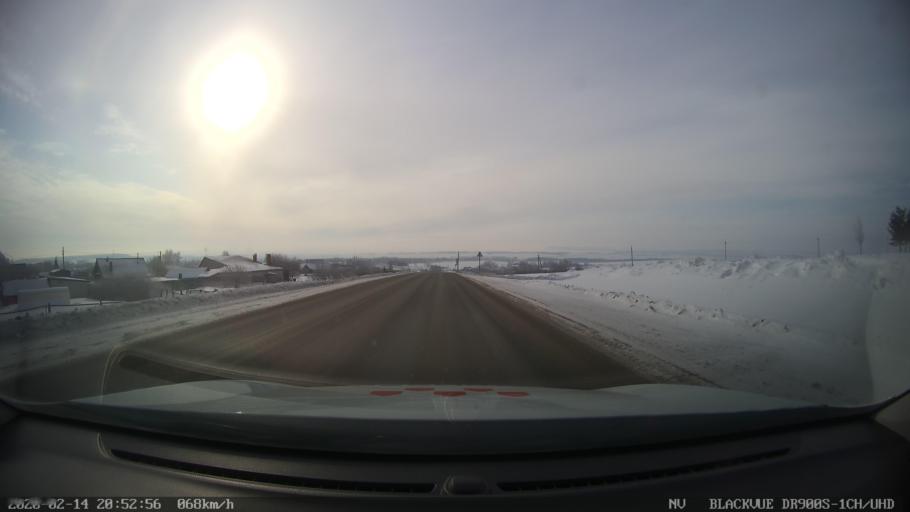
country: RU
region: Tatarstan
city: Kuybyshevskiy Zaton
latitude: 55.1992
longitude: 49.2490
